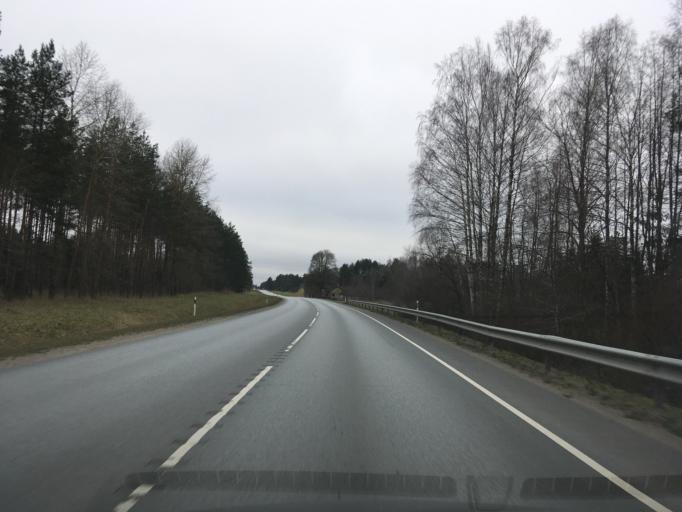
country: EE
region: Laeaene-Virumaa
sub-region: Viru-Nigula vald
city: Kunda
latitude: 59.4081
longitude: 26.6390
